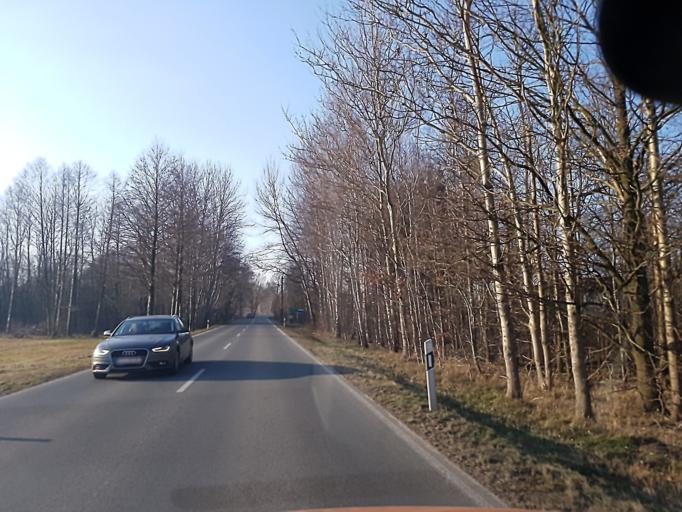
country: DE
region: Brandenburg
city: Ruckersdorf
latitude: 51.5963
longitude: 13.5555
